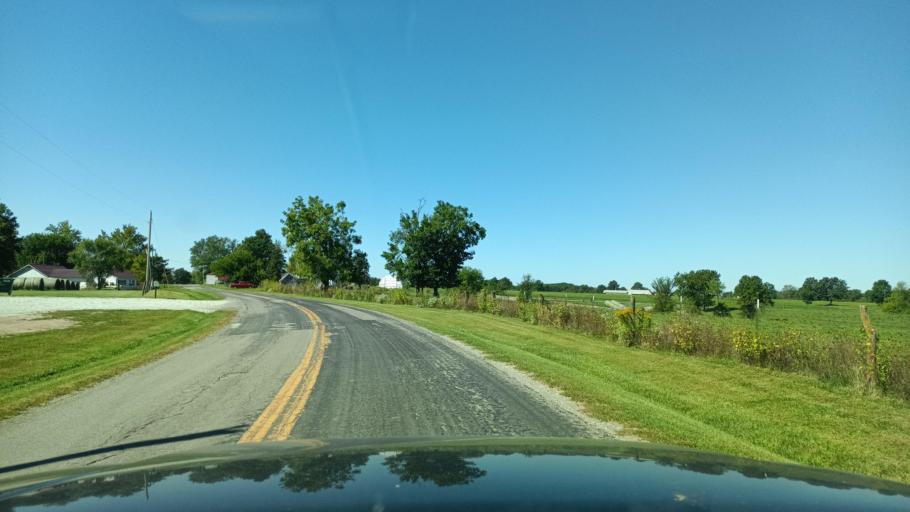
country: US
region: Missouri
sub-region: Scotland County
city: Memphis
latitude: 40.3539
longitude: -92.3001
